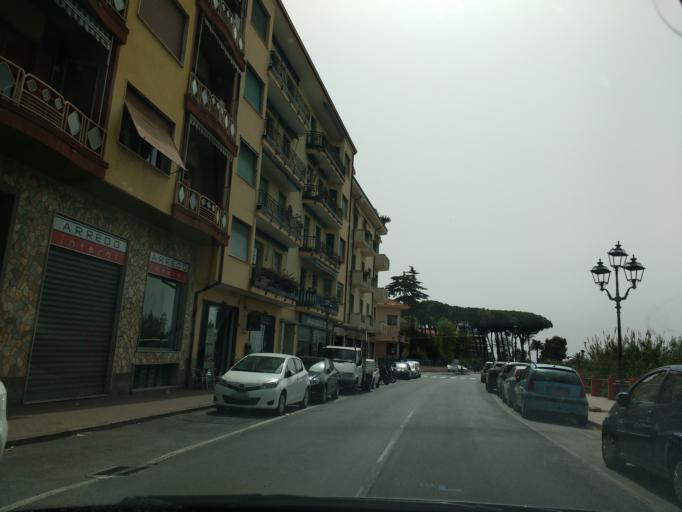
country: IT
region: Liguria
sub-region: Provincia di Imperia
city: Ventimiglia
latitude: 43.7912
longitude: 7.6066
